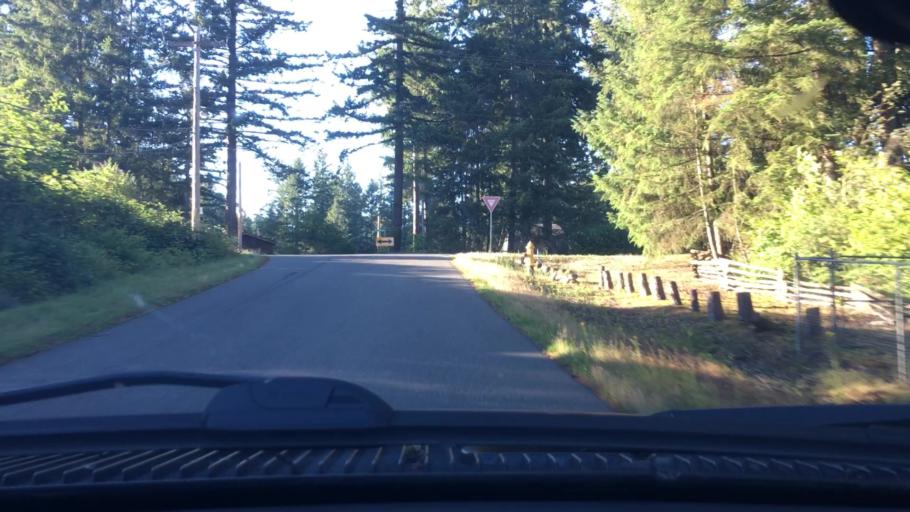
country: US
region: Washington
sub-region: King County
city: Lake Morton-Berrydale
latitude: 47.3468
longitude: -122.0734
